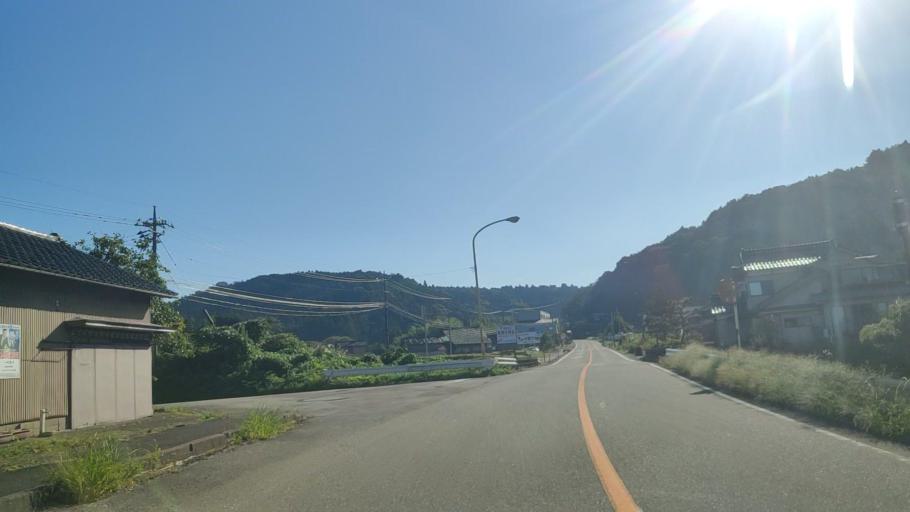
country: JP
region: Ishikawa
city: Nanao
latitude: 37.1434
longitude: 136.8718
